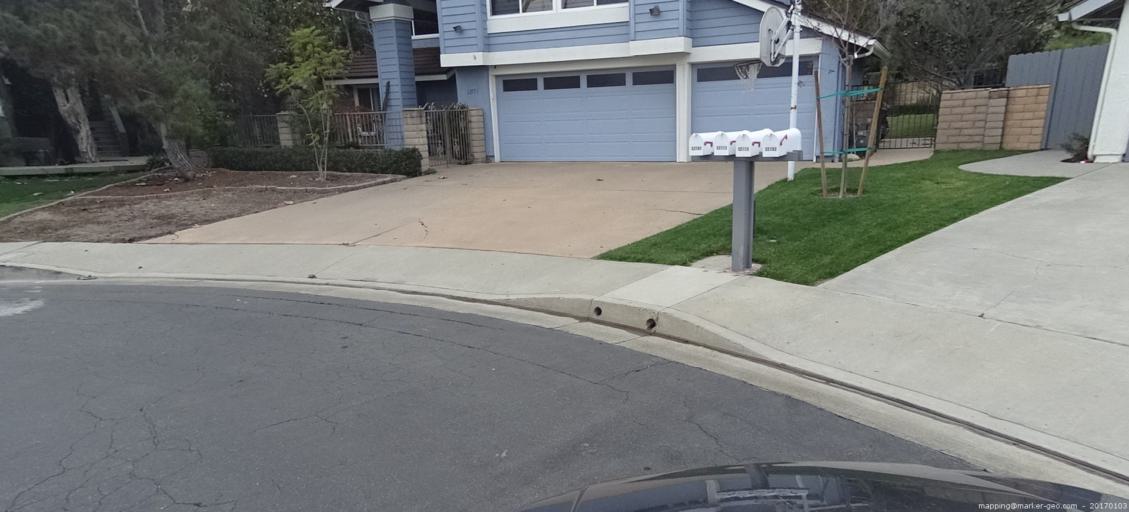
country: US
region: California
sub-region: Orange County
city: Dana Point
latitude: 33.4869
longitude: -117.6877
